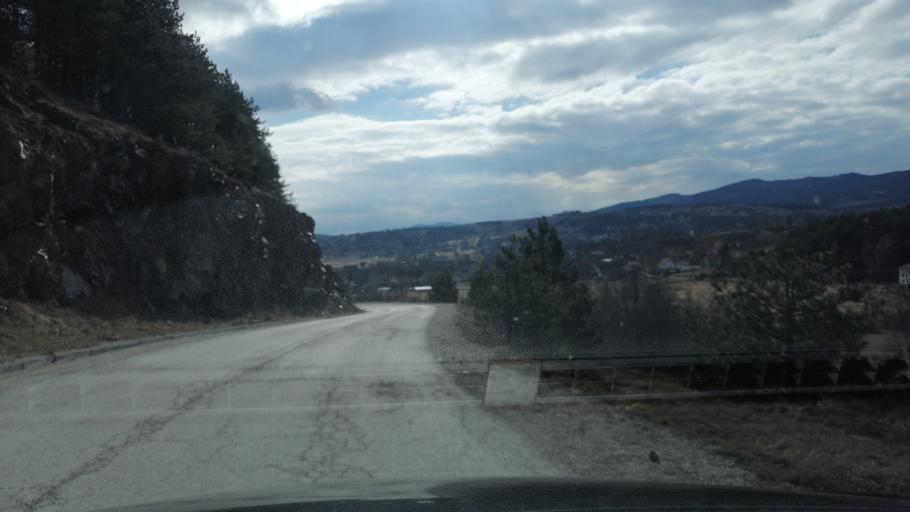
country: RS
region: Central Serbia
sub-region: Zlatiborski Okrug
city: Bajina Basta
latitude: 43.8615
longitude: 19.5783
